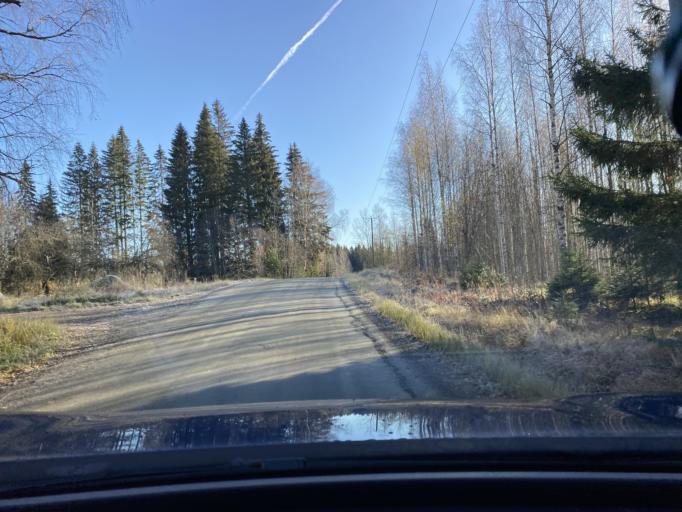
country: FI
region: Pirkanmaa
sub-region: Etelae-Pirkanmaa
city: Kylmaekoski
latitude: 61.0405
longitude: 23.7695
